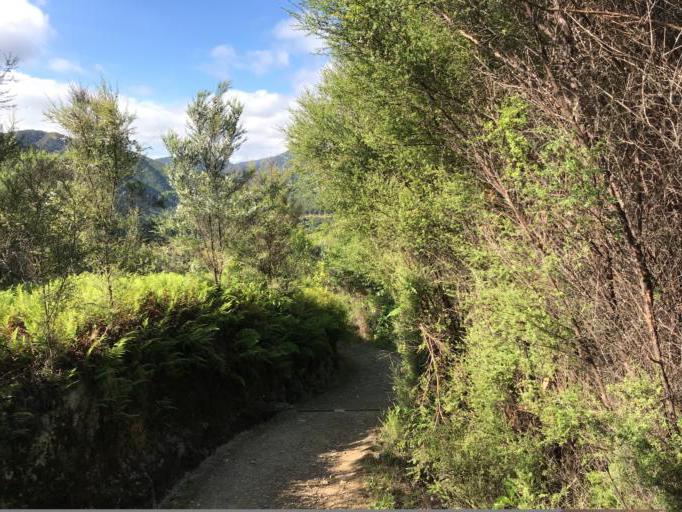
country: NZ
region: Wellington
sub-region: Kapiti Coast District
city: Otaki
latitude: -40.8758
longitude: 175.2347
